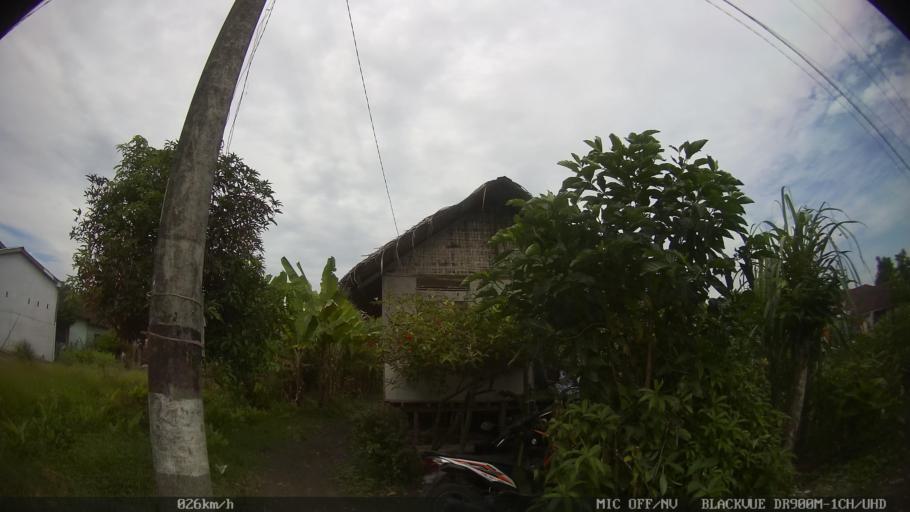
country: ID
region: North Sumatra
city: Sunggal
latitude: 3.6526
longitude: 98.5923
